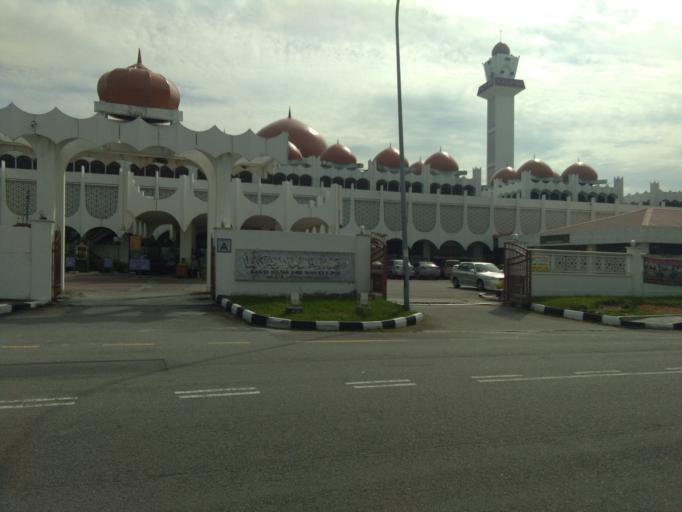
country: MY
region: Perak
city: Ipoh
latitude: 4.5957
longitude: 101.0754
